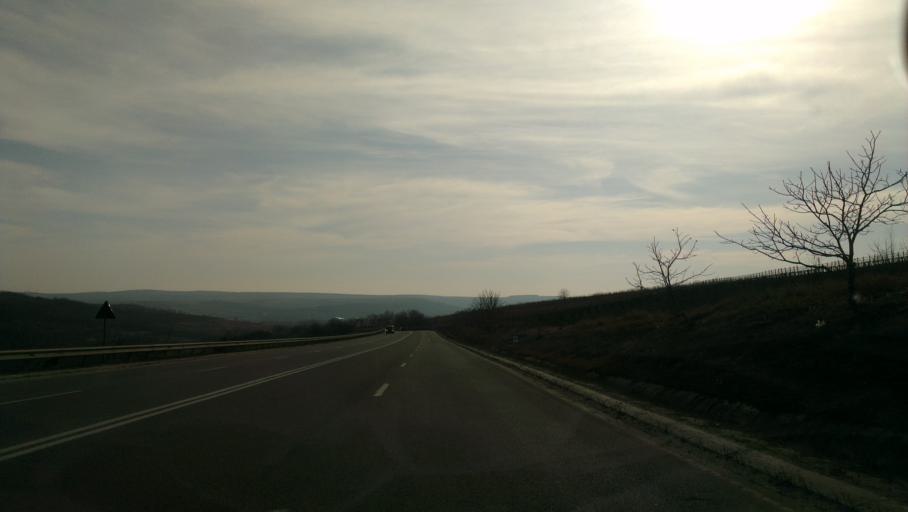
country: MD
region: Laloveni
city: Ialoveni
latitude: 46.9418
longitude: 28.7054
